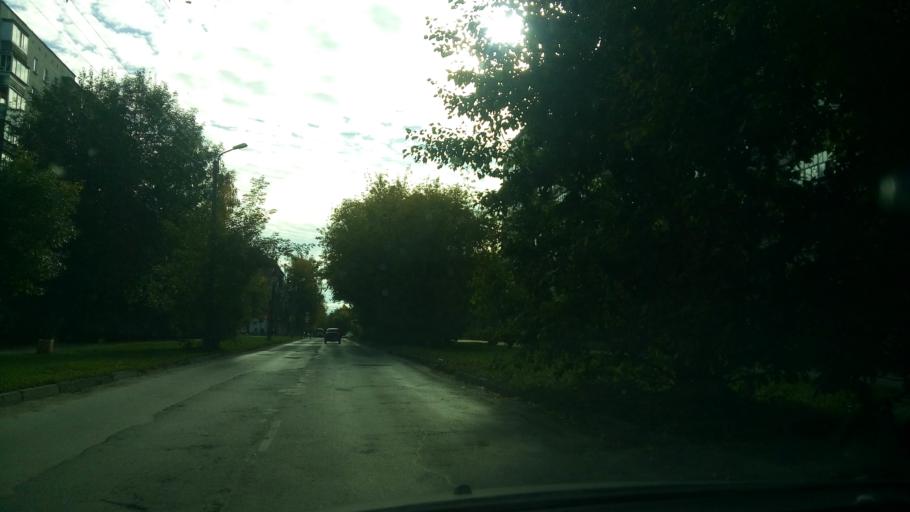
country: RU
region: Sverdlovsk
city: Yekaterinburg
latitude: 56.9039
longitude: 60.6045
